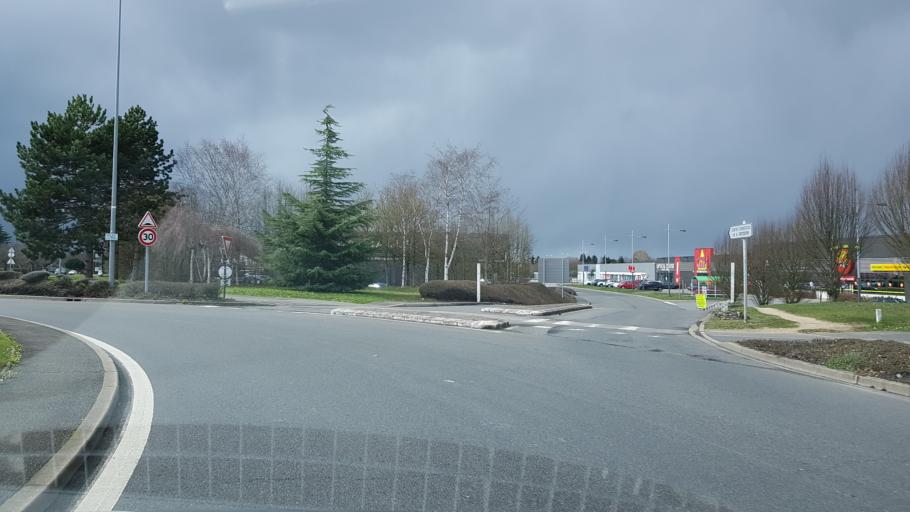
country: FR
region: Ile-de-France
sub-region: Departement des Yvelines
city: Rambouillet
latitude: 48.6448
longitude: 1.8482
